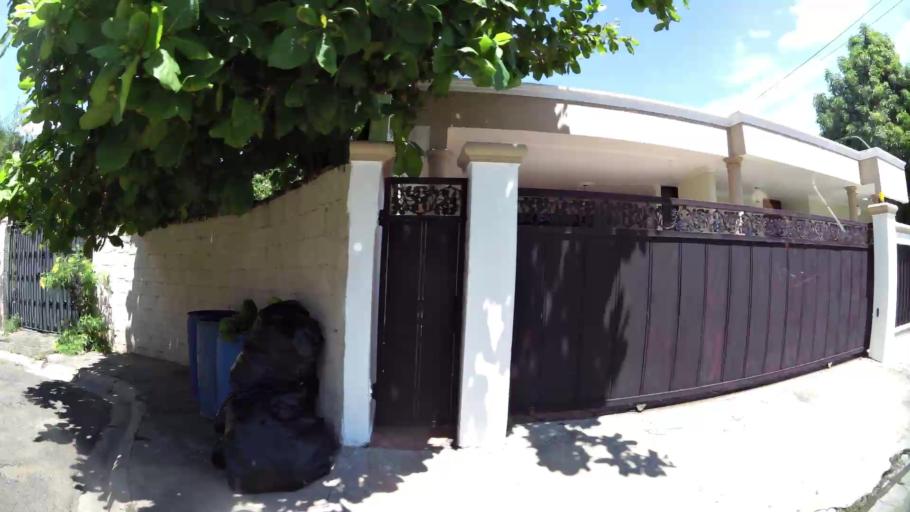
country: DO
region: Santiago
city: Santiago de los Caballeros
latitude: 19.4625
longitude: -70.6825
